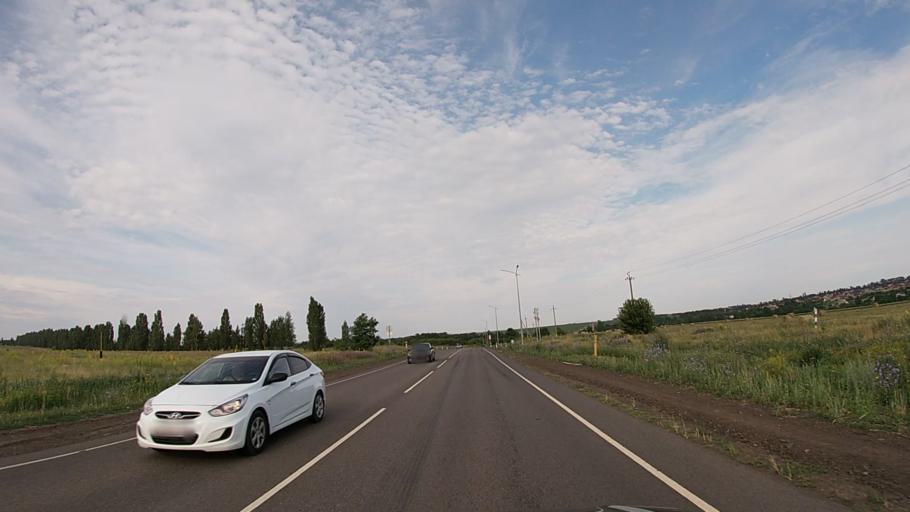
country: RU
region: Belgorod
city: Severnyy
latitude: 50.6652
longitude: 36.5318
